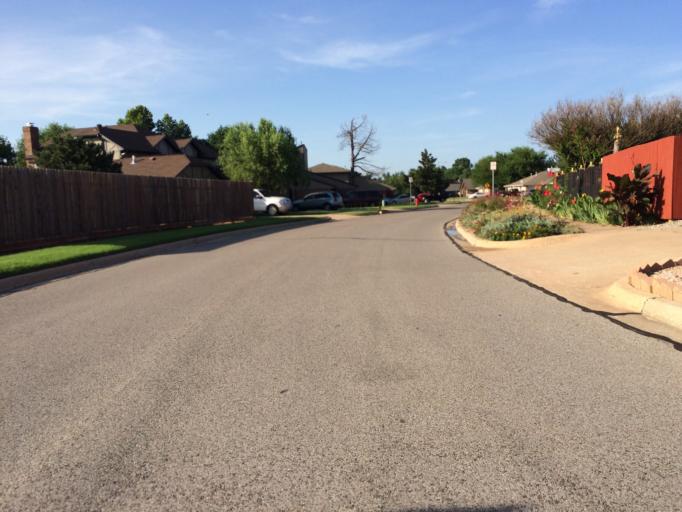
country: US
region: Oklahoma
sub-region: Cleveland County
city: Norman
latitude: 35.2224
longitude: -97.5002
